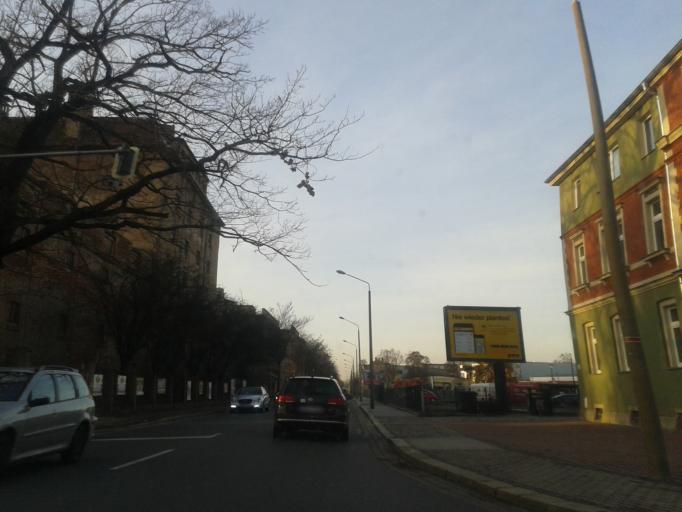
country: DE
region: Saxony
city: Heidenau
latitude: 51.0035
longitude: 13.8251
